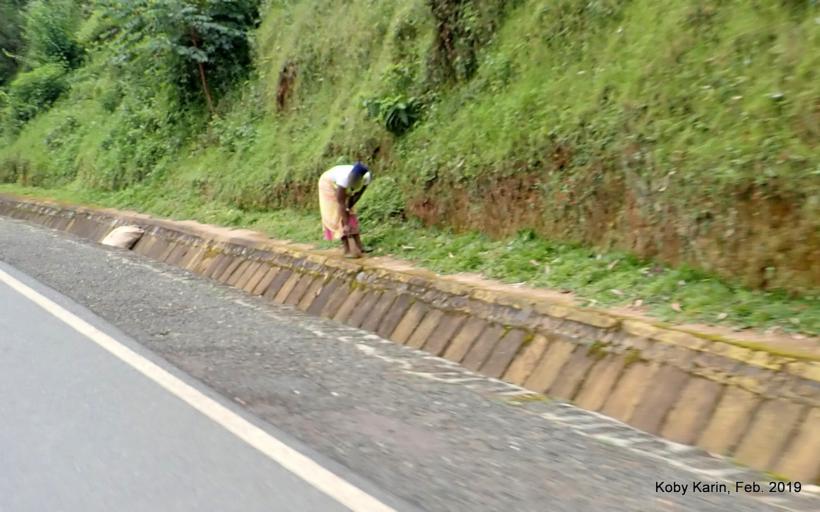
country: RW
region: Northern Province
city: Musanze
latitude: -1.5739
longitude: 29.7182
